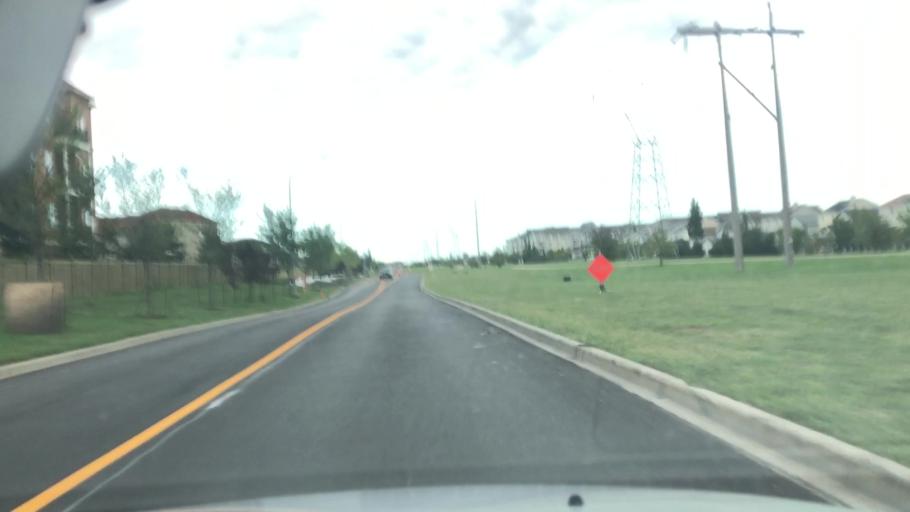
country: CA
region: Alberta
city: St. Albert
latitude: 53.6146
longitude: -113.5649
